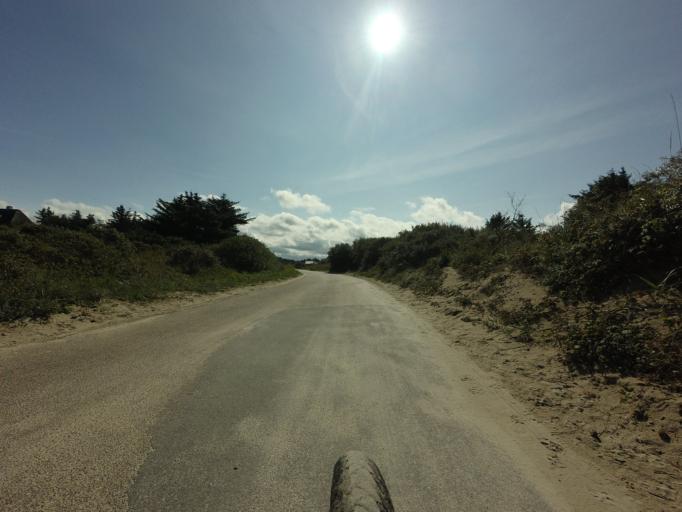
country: DK
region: North Denmark
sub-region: Hjorring Kommune
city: Hirtshals
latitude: 57.5889
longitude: 10.0278
